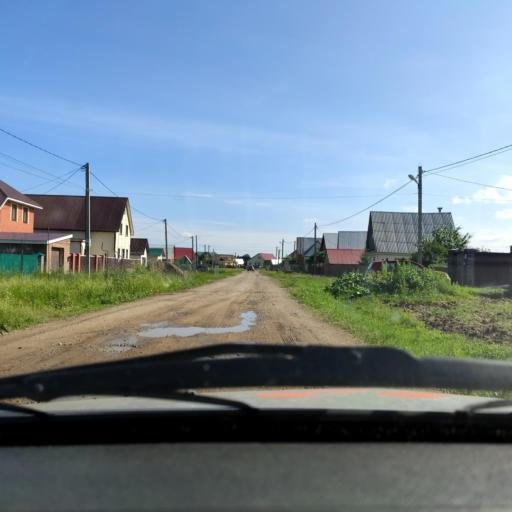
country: RU
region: Bashkortostan
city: Iglino
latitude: 54.7988
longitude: 56.2989
